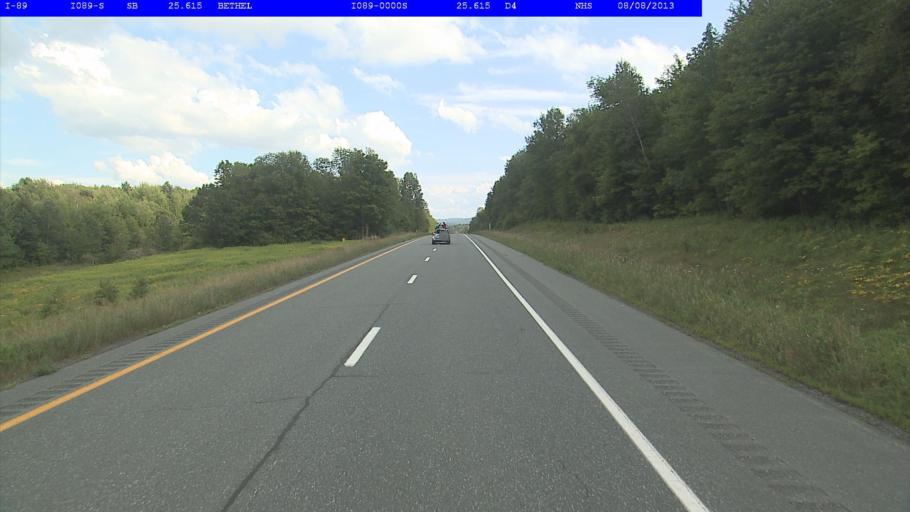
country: US
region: Vermont
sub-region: Orange County
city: Randolph
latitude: 43.8706
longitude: -72.6118
